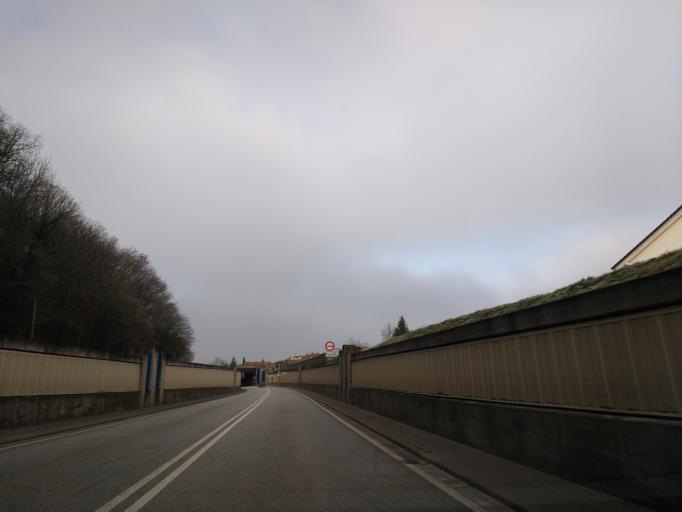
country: DE
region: Baden-Wuerttemberg
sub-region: Freiburg Region
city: Oberkirch
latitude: 48.5236
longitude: 8.0769
